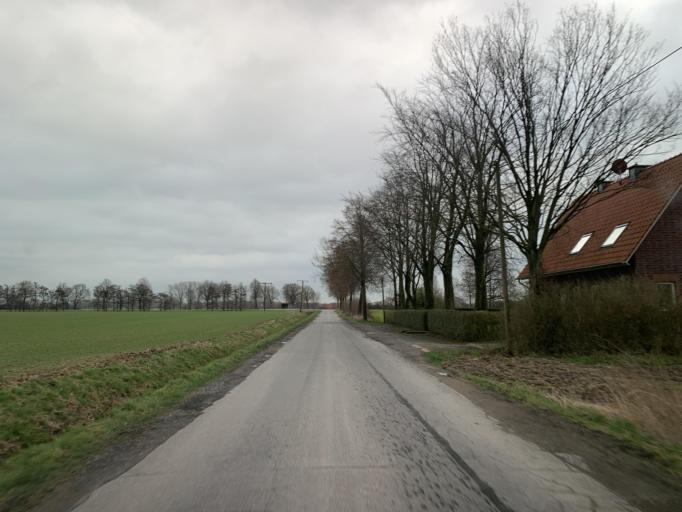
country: DE
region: North Rhine-Westphalia
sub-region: Regierungsbezirk Munster
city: Senden
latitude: 51.8066
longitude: 7.4819
